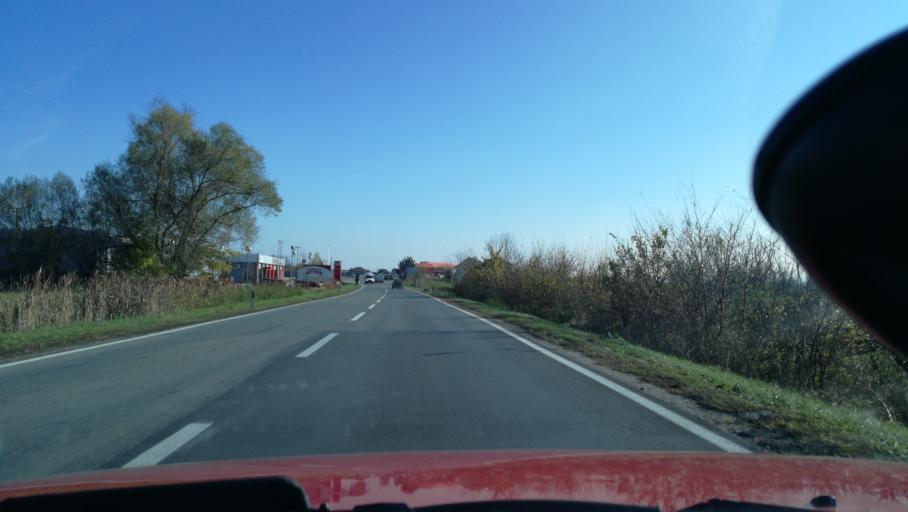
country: RS
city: Prislonica
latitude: 43.9025
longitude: 20.4138
